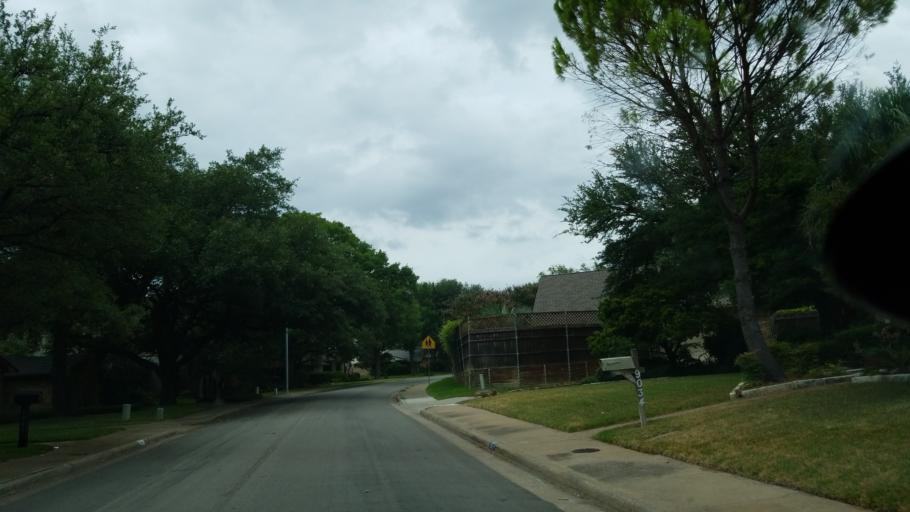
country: US
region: Texas
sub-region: Dallas County
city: Richardson
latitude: 32.9002
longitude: -96.7330
